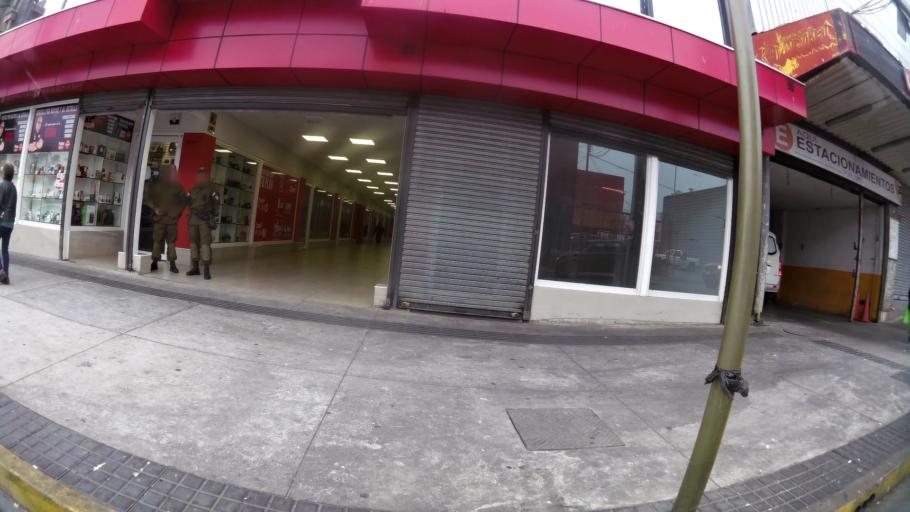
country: CL
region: Biobio
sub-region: Provincia de Concepcion
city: Concepcion
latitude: -36.8240
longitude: -73.0530
